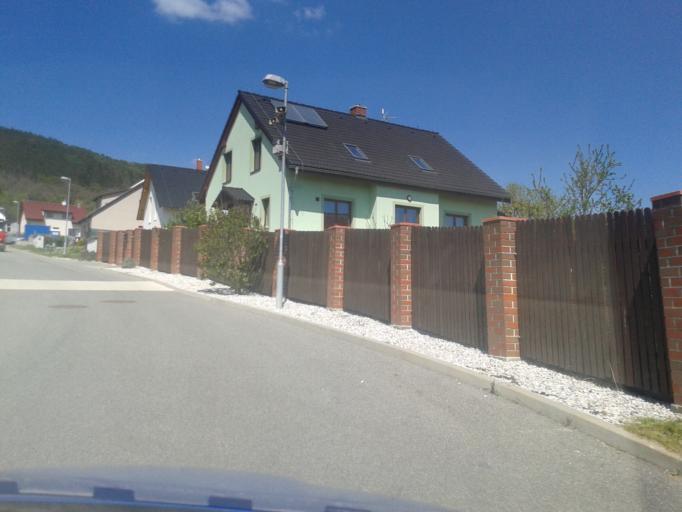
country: CZ
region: Central Bohemia
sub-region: Okres Beroun
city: Kraluv Dvur
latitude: 49.9548
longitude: 14.0311
